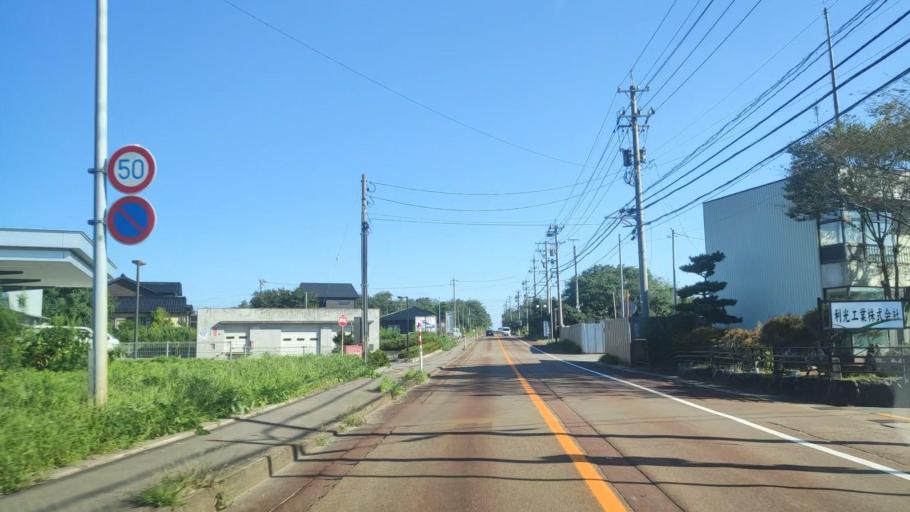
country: JP
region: Ishikawa
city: Hakui
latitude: 36.8632
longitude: 136.7710
